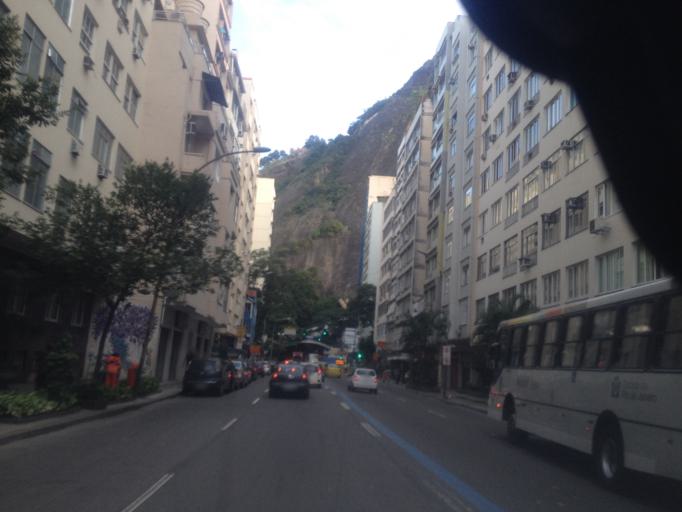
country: BR
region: Rio de Janeiro
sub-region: Rio De Janeiro
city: Rio de Janeiro
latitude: -22.9765
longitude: -43.1925
